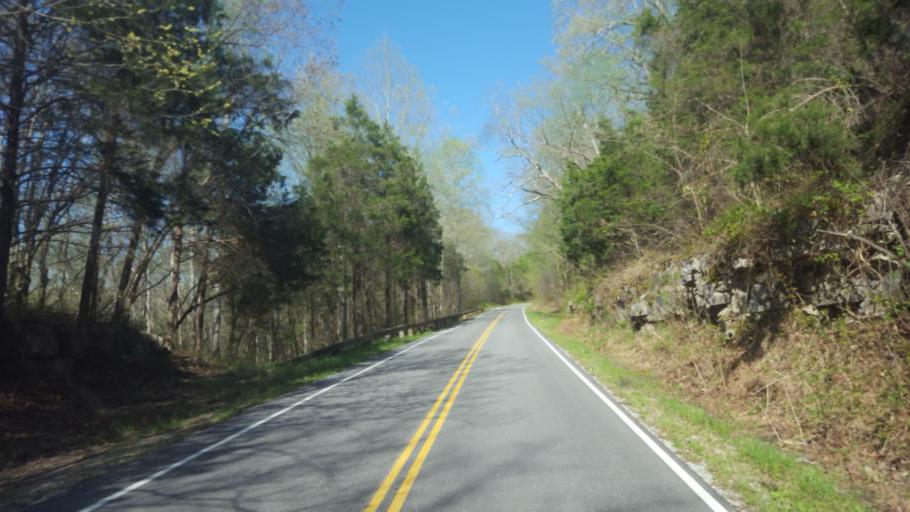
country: US
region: Kentucky
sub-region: Edmonson County
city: Brownsville
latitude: 37.1571
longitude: -86.1582
